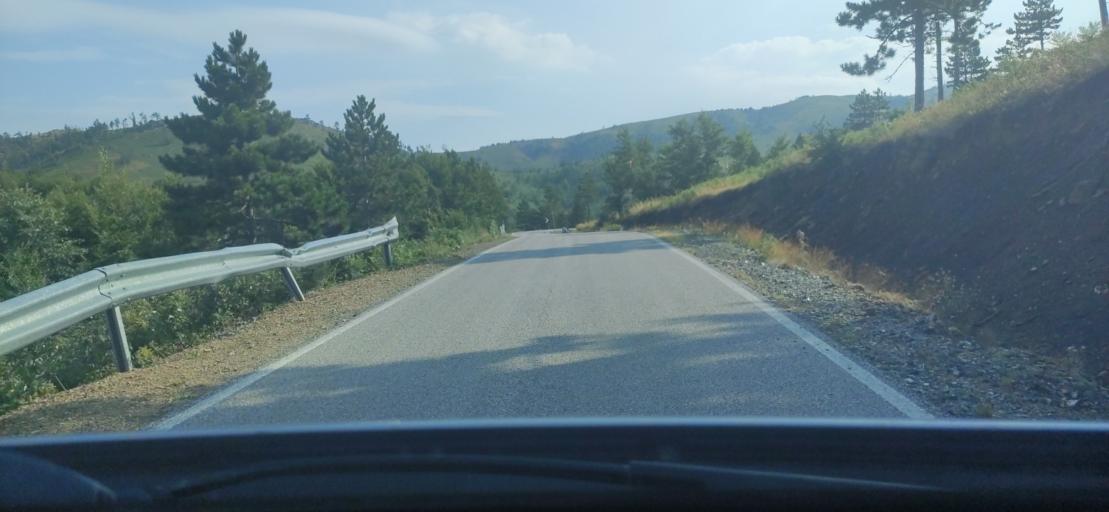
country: AL
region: Shkoder
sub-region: Rrethi i Pukes
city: Iballe
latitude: 42.1724
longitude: 20.0244
